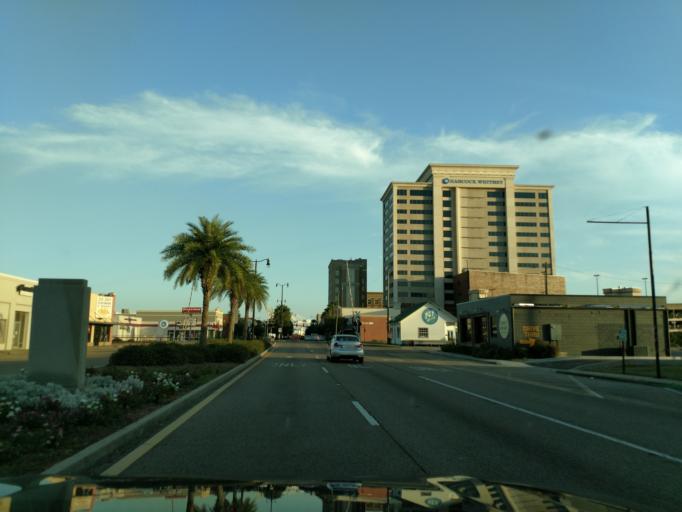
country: US
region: Mississippi
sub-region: Harrison County
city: Gulfport
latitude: 30.3704
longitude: -89.0930
